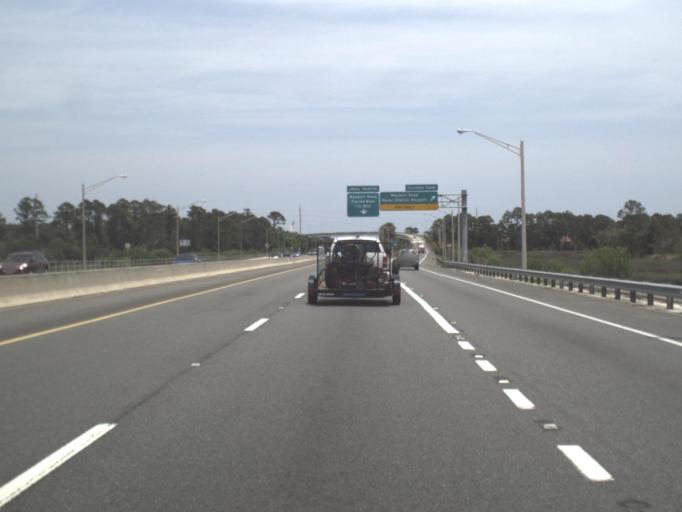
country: US
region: Florida
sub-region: Duval County
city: Atlantic Beach
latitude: 30.3242
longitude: -81.4286
